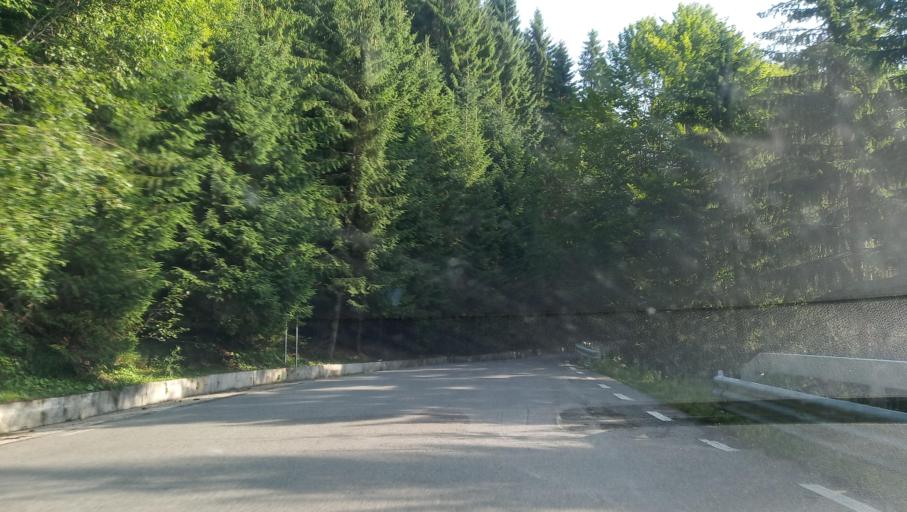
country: RO
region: Prahova
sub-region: Oras Sinaia
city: Sinaia
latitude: 45.3180
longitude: 25.4870
